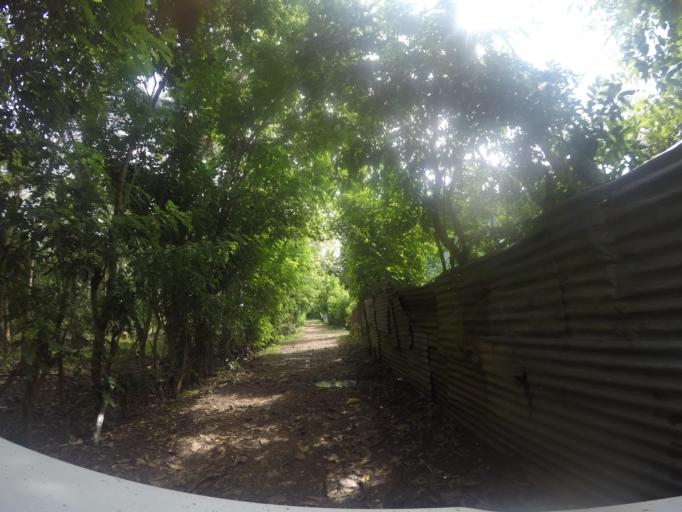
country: TL
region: Lautem
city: Lospalos
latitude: -8.5042
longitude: 127.0084
